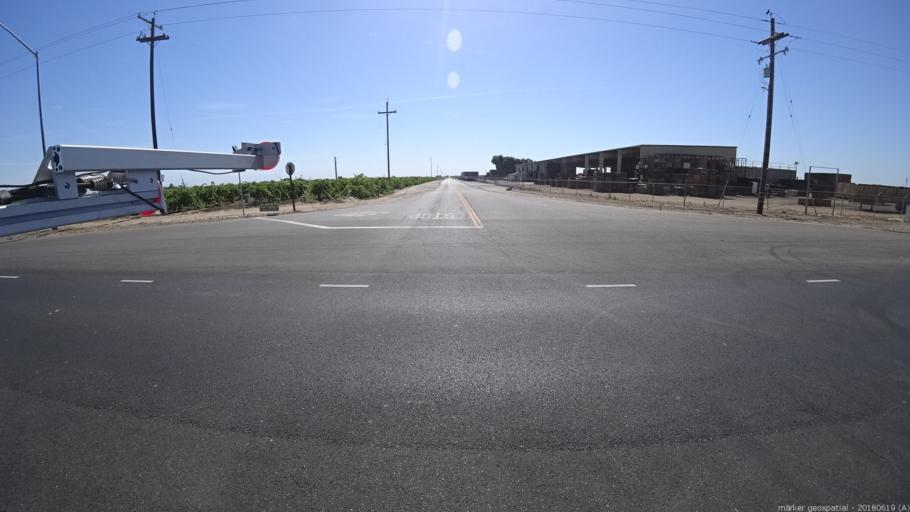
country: US
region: California
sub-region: Fresno County
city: Biola
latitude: 36.8368
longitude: -120.0559
